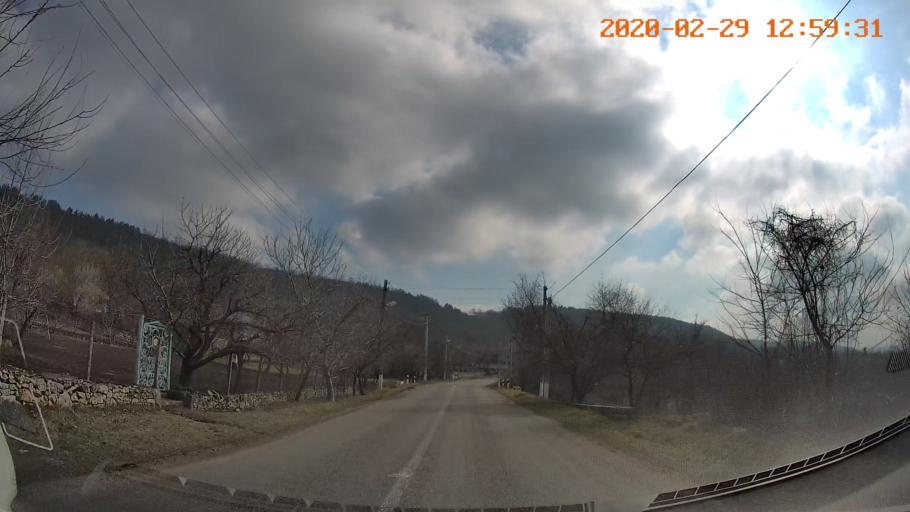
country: MD
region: Telenesti
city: Camenca
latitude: 48.0613
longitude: 28.7244
